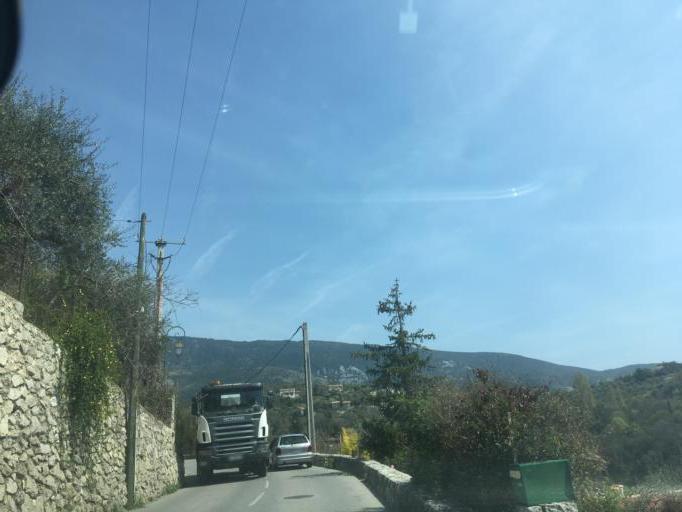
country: FR
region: Provence-Alpes-Cote d'Azur
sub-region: Departement des Alpes-Maritimes
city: Levens
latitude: 43.8506
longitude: 7.2240
